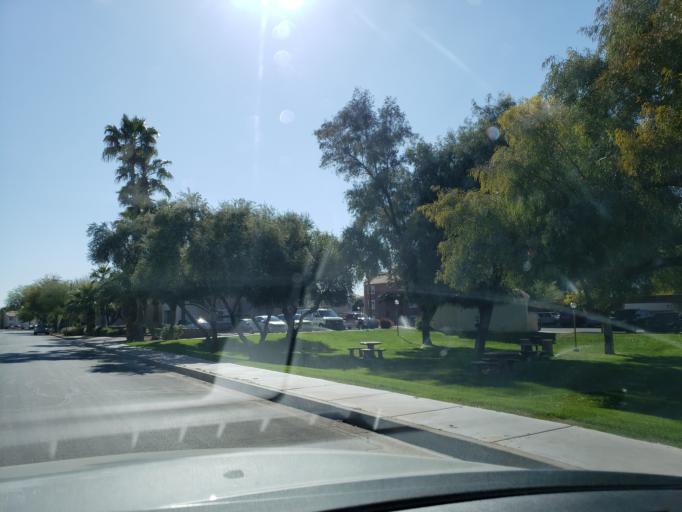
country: US
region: Arizona
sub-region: Maricopa County
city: Glendale
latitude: 33.5846
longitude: -112.1875
